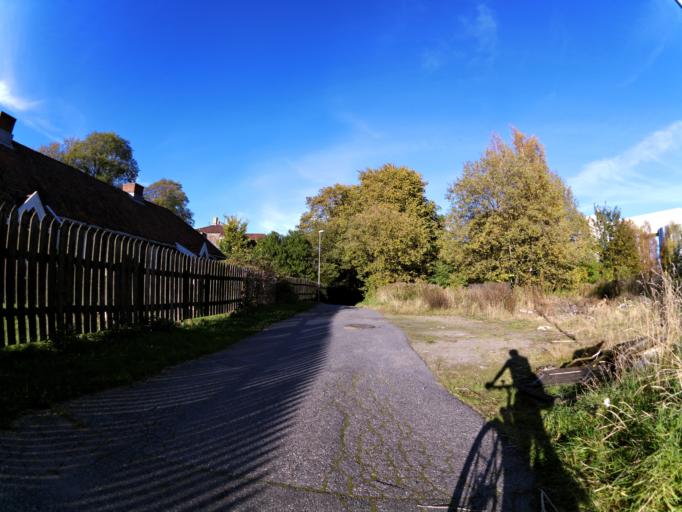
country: NO
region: Ostfold
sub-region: Sarpsborg
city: Sarpsborg
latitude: 59.2786
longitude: 11.1249
